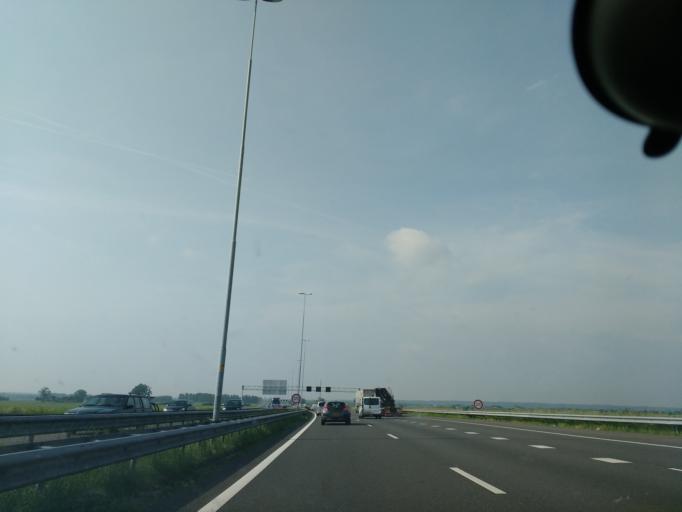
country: NL
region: Gelderland
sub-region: Gemeente Overbetuwe
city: Valburg
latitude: 51.9184
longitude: 5.7722
